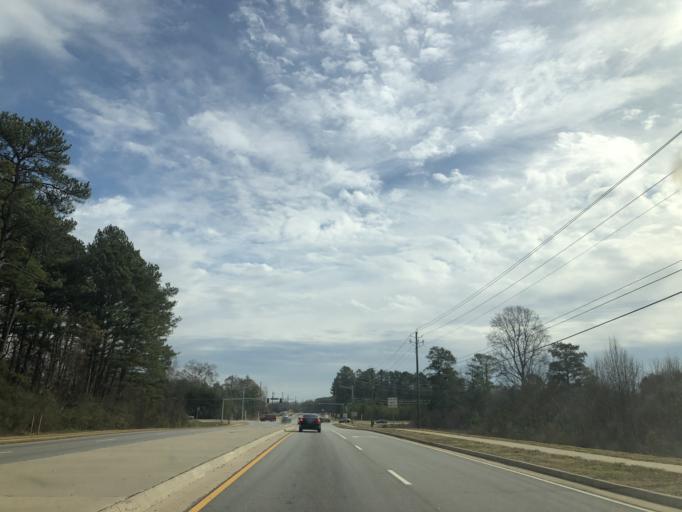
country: US
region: Georgia
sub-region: Clayton County
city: Conley
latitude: 33.6312
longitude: -84.2845
